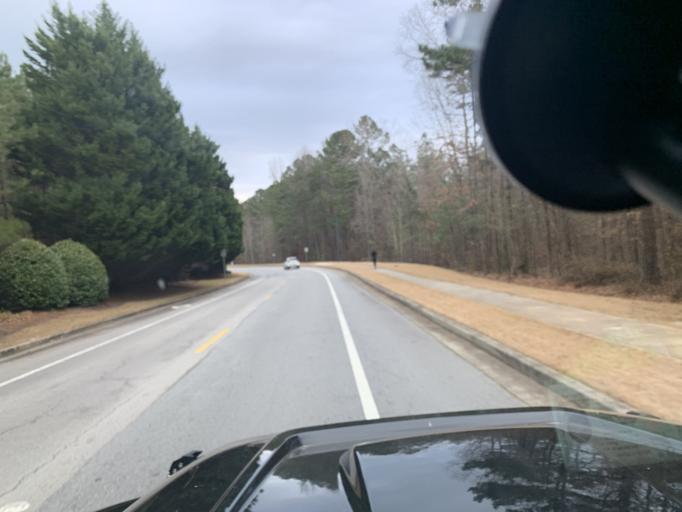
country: US
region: Georgia
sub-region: Cherokee County
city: Woodstock
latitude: 34.0893
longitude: -84.4577
